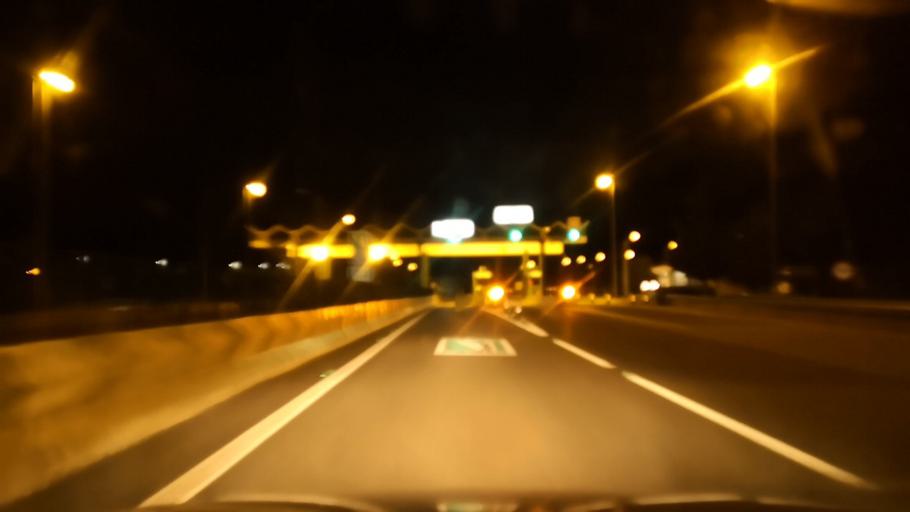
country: PT
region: Evora
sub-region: Estremoz
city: Estremoz
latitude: 38.8231
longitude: -7.6081
